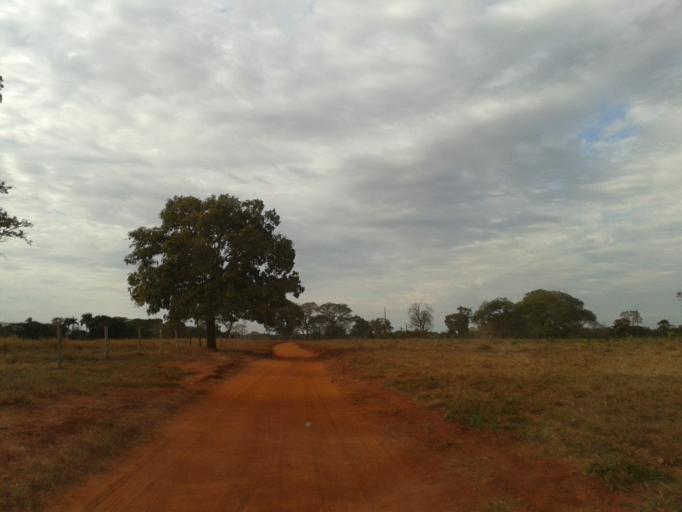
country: BR
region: Minas Gerais
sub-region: Santa Vitoria
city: Santa Vitoria
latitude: -18.7420
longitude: -50.2137
